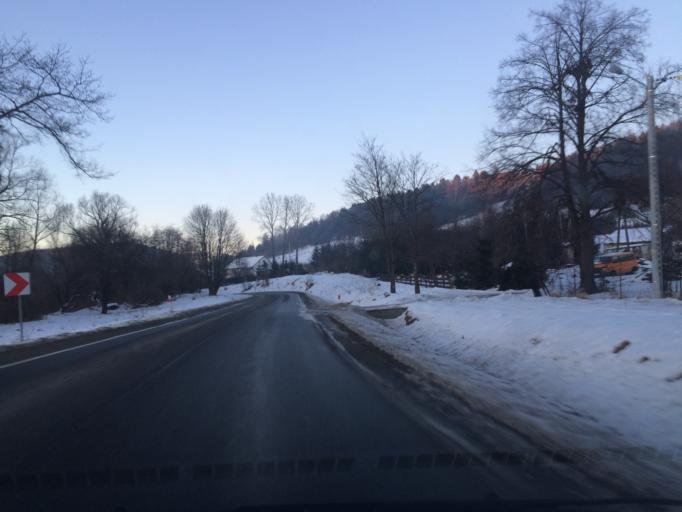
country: PL
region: Subcarpathian Voivodeship
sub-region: Powiat bieszczadzki
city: Czarna
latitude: 49.3798
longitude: 22.6414
